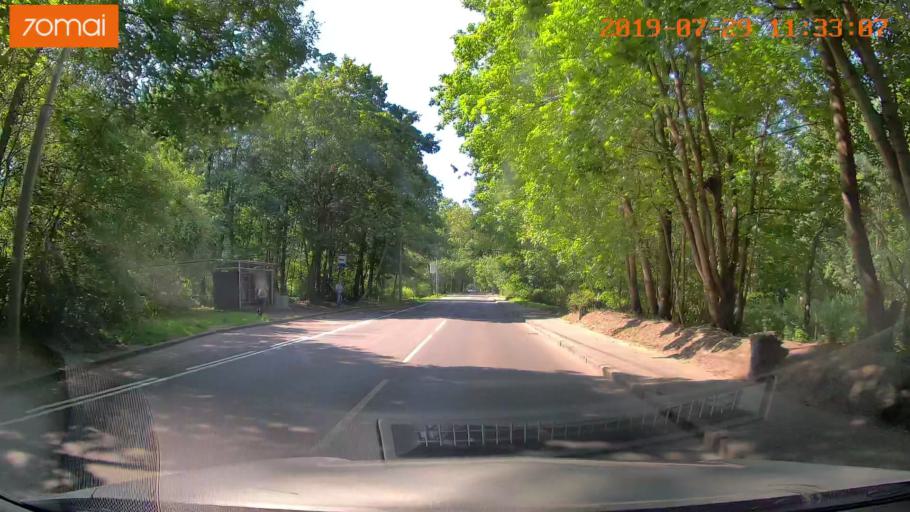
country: RU
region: Kaliningrad
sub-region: Gorod Kaliningrad
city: Kaliningrad
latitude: 54.6669
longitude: 20.5430
